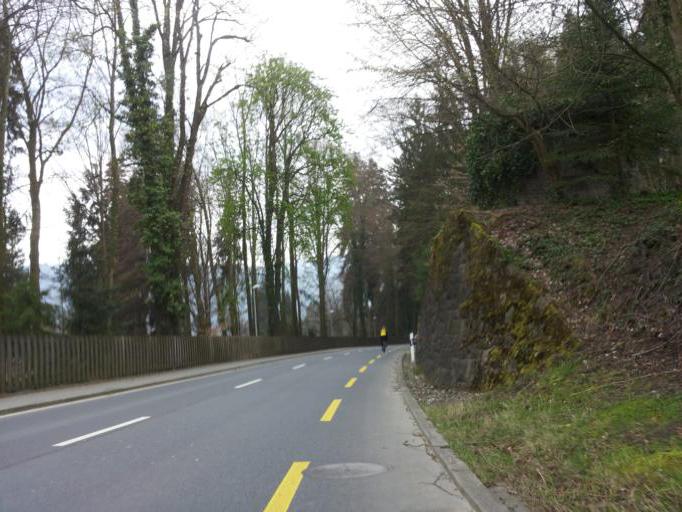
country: CH
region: Lucerne
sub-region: Lucerne-Land District
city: Meierskappel
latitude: 47.1374
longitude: 8.4640
